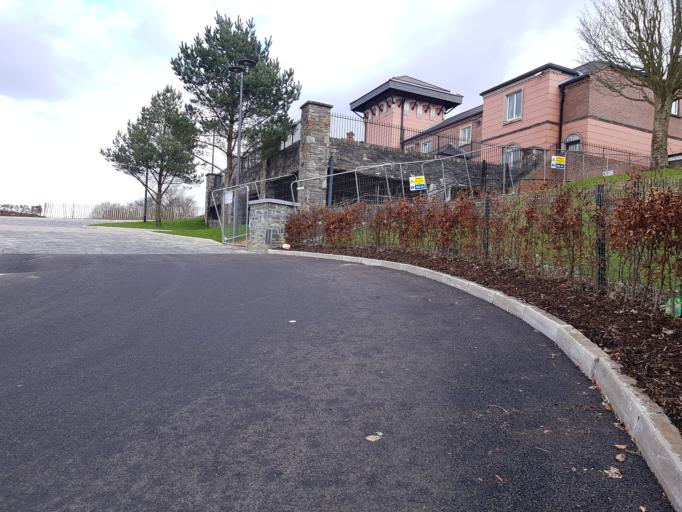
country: GB
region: Northern Ireland
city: Londonderry County Borough
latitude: 54.9935
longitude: -7.3267
